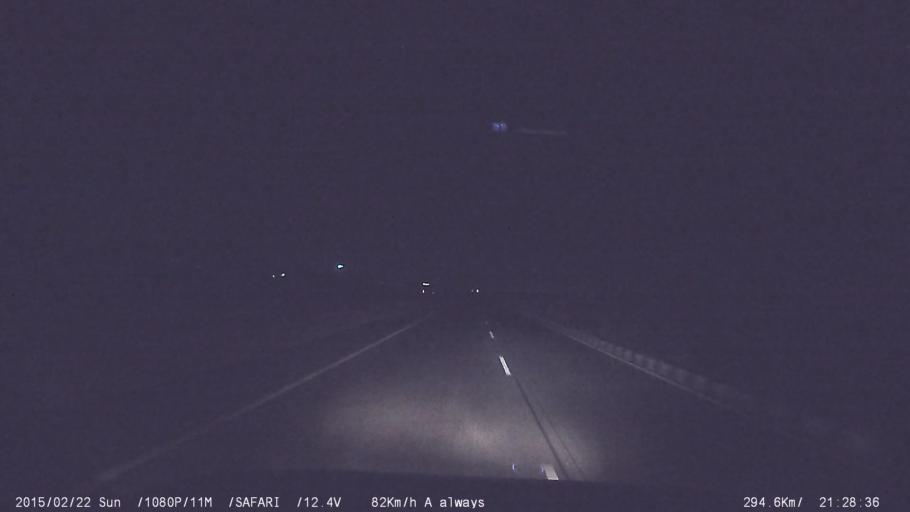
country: IN
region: Tamil Nadu
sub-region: Karur
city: Karur
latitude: 10.9262
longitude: 78.0505
